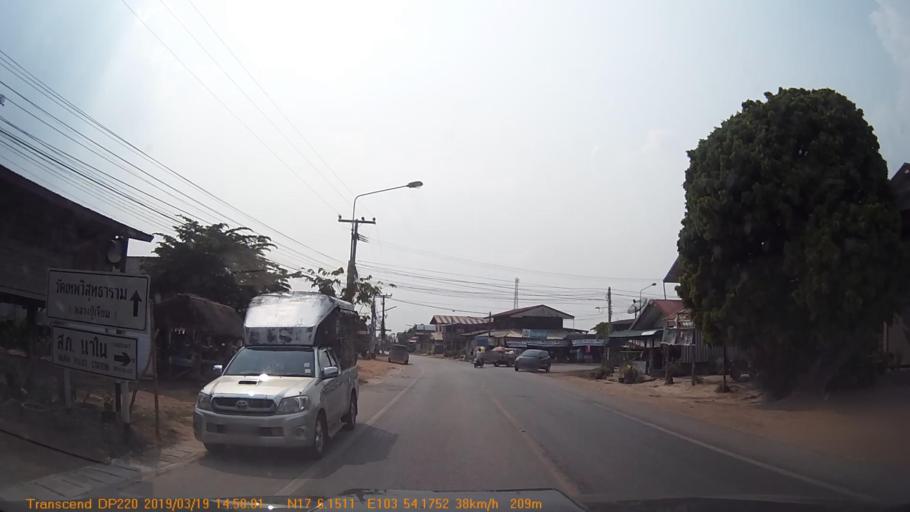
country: TH
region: Sakon Nakhon
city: Kut Bak
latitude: 17.1026
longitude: 103.9028
